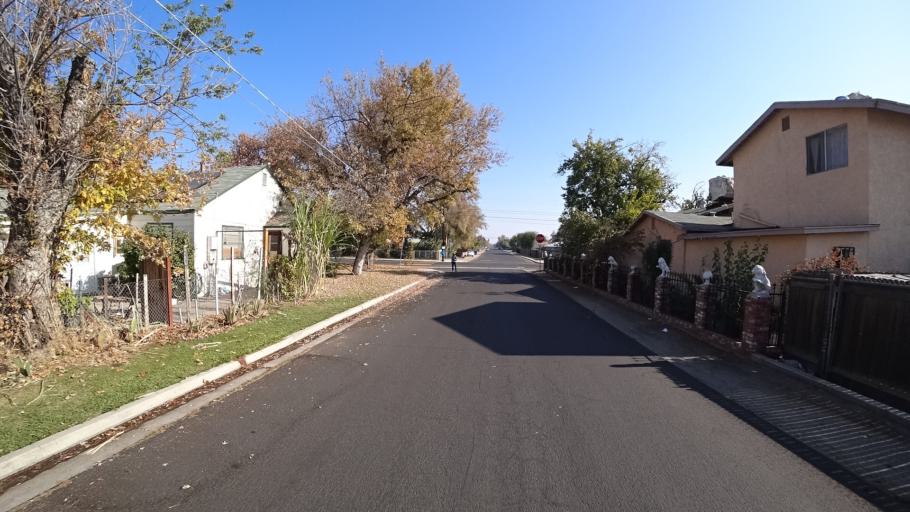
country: US
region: California
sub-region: Kern County
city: Bakersfield
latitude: 35.3431
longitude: -119.0293
